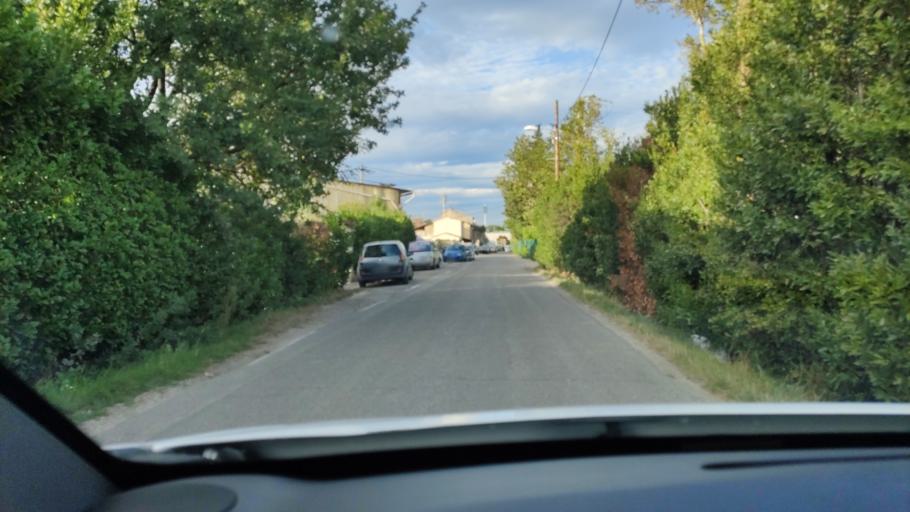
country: FR
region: Provence-Alpes-Cote d'Azur
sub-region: Departement du Vaucluse
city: Montfavet
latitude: 43.9232
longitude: 4.8437
